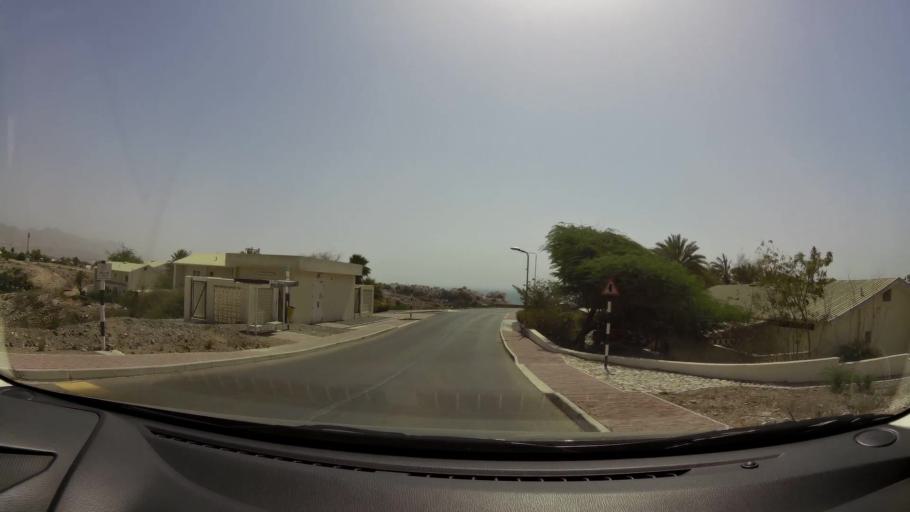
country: OM
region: Muhafazat Masqat
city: Muscat
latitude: 23.6340
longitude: 58.4949
